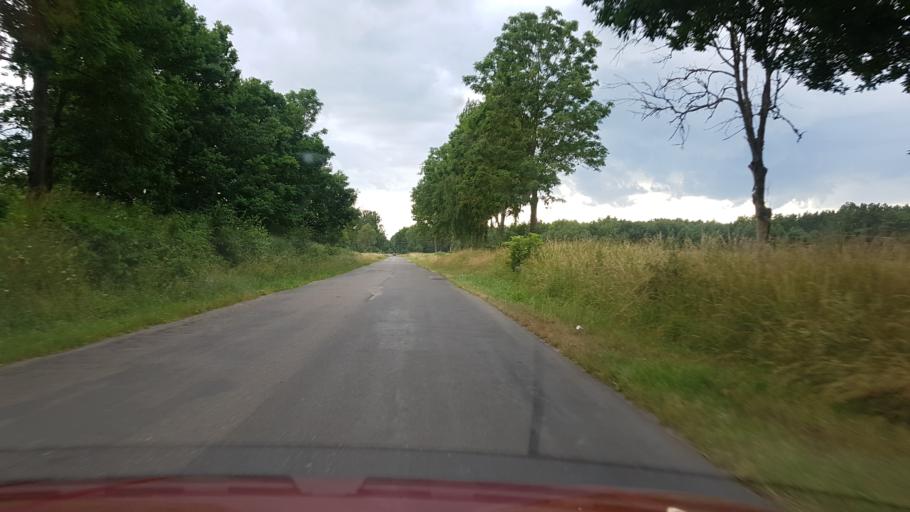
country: PL
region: West Pomeranian Voivodeship
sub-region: Powiat gryficki
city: Gryfice
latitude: 53.8744
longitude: 15.1297
